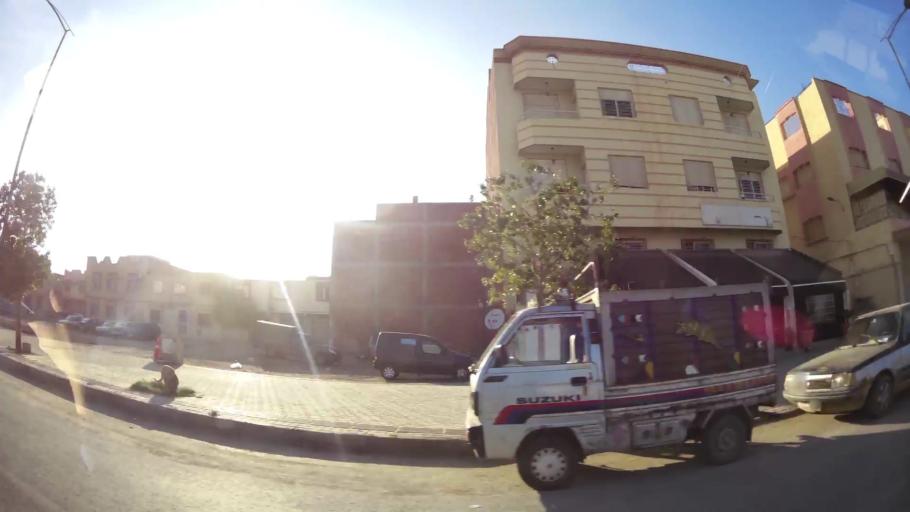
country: MA
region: Oriental
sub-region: Oujda-Angad
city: Oujda
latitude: 34.7078
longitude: -1.8920
